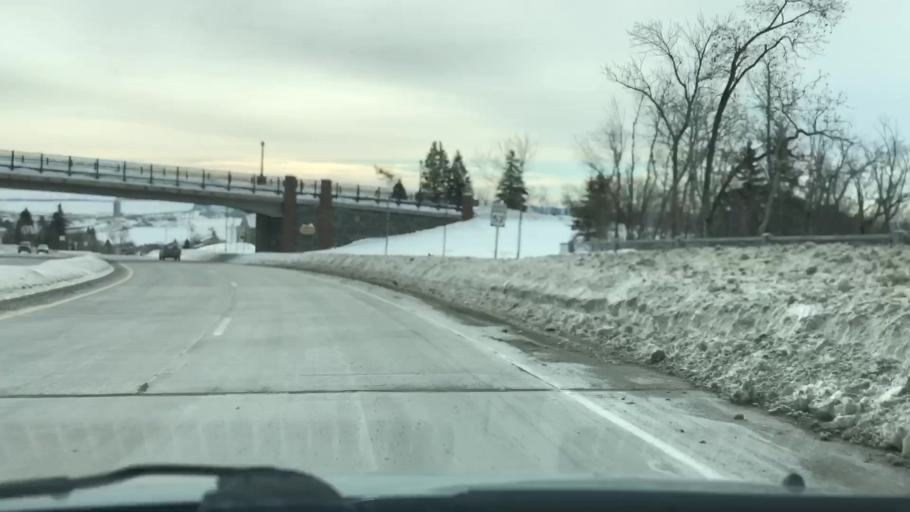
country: US
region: Minnesota
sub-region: Saint Louis County
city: Duluth
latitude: 46.7744
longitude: -92.1427
